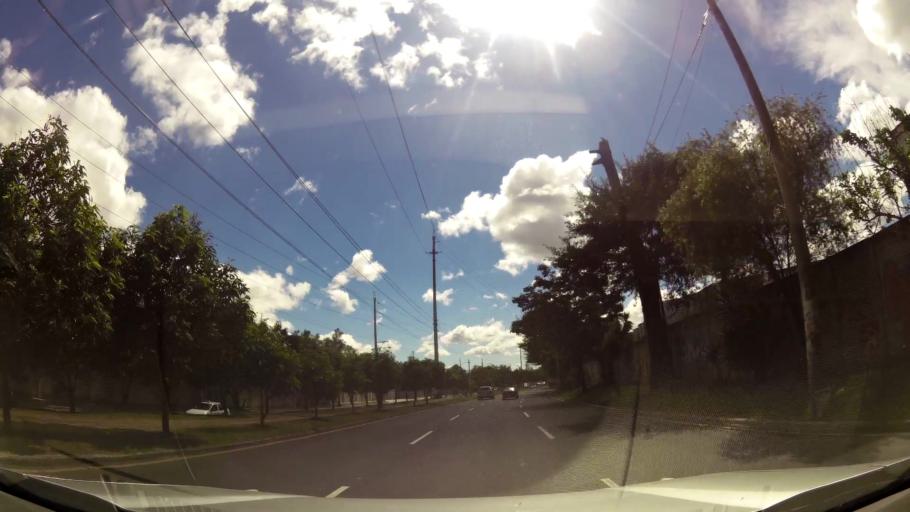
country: GT
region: Guatemala
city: Santa Catarina Pinula
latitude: 14.5732
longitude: -90.5423
